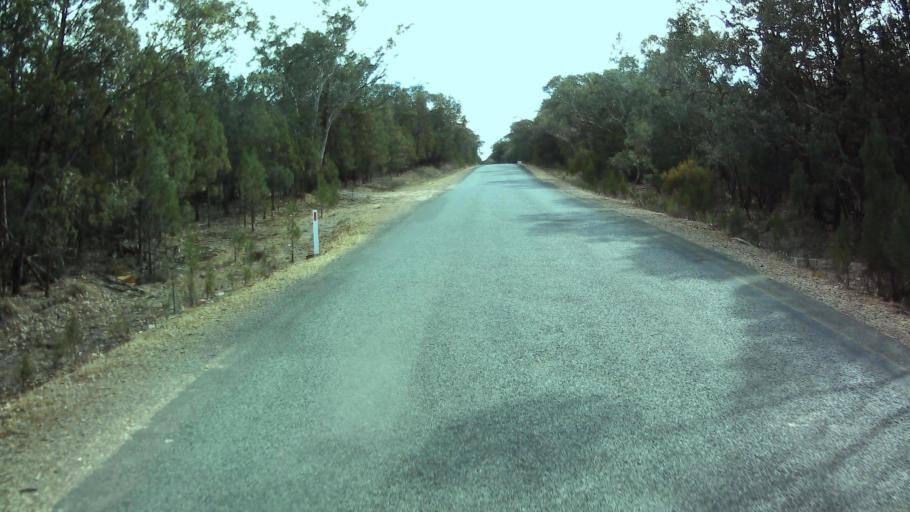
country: AU
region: New South Wales
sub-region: Weddin
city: Grenfell
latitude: -33.8956
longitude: 148.1860
